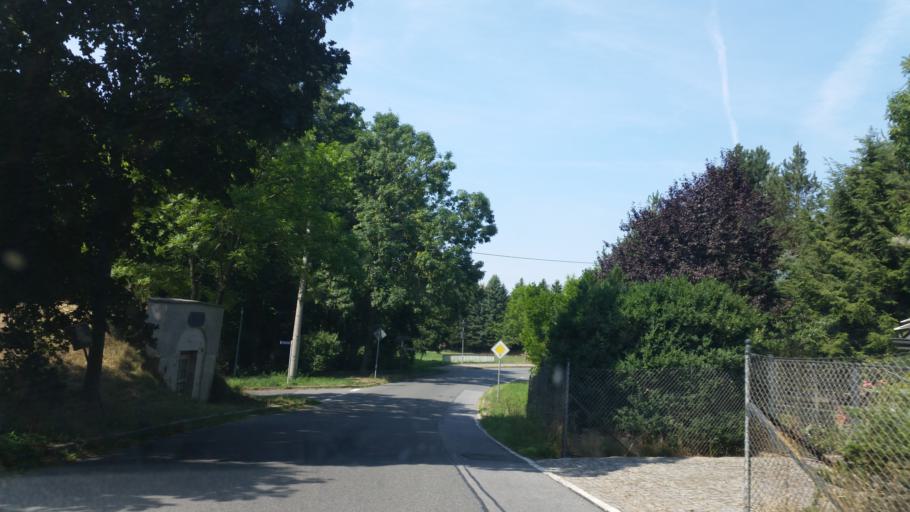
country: DE
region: Saxony
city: Klipphausen
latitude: 51.0700
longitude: 13.5319
